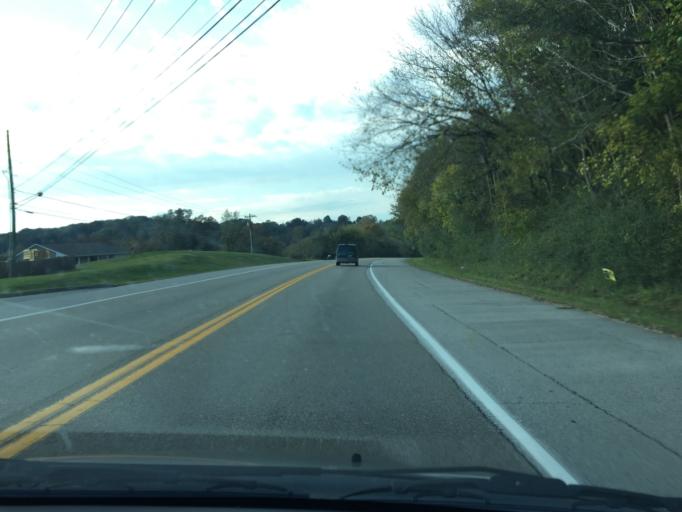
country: US
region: Tennessee
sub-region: Loudon County
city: Loudon
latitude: 35.7218
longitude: -84.3743
